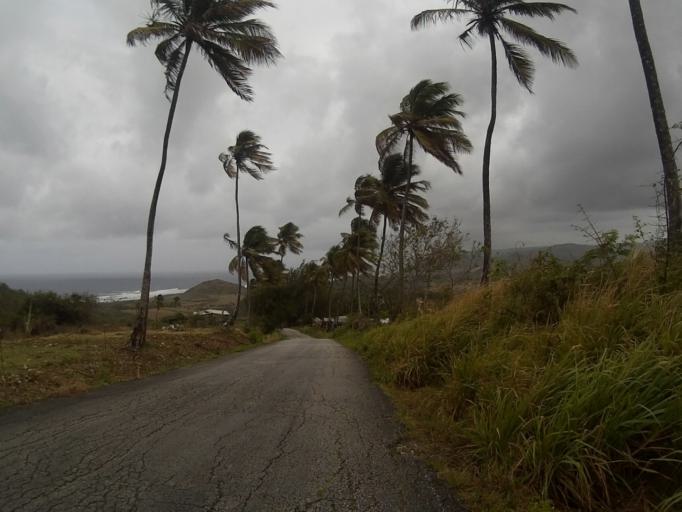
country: BB
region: Saint Andrew
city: Greenland
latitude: 13.2699
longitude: -59.5762
